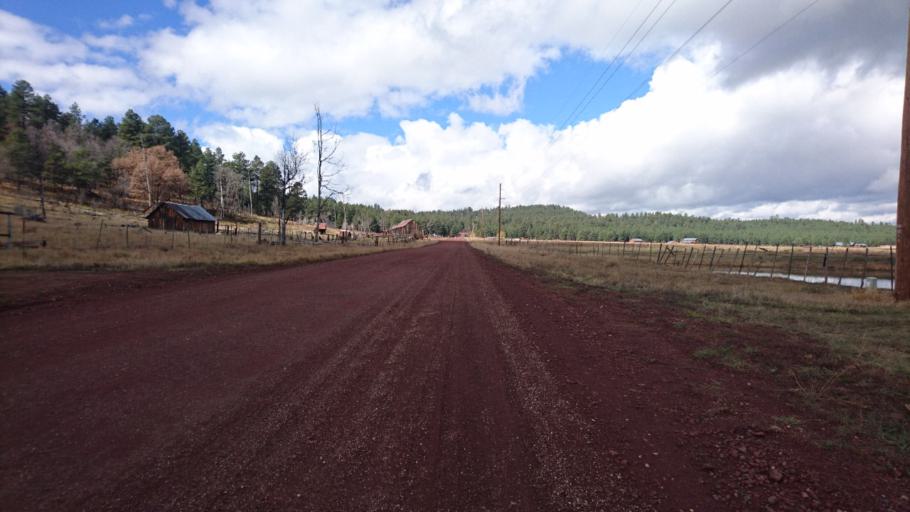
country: US
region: Arizona
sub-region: Coconino County
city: Parks
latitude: 35.2704
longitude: -111.8877
